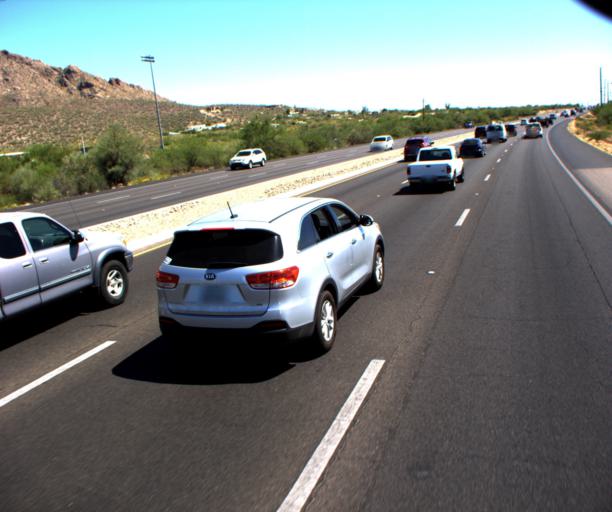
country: US
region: Arizona
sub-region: Pima County
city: Oro Valley
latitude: 32.3795
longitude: -110.9644
